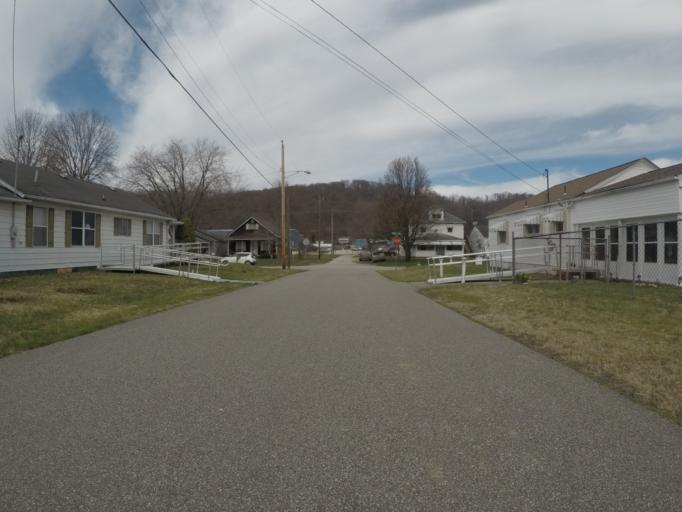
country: US
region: West Virginia
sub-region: Cabell County
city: Pea Ridge
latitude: 38.4136
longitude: -82.3706
